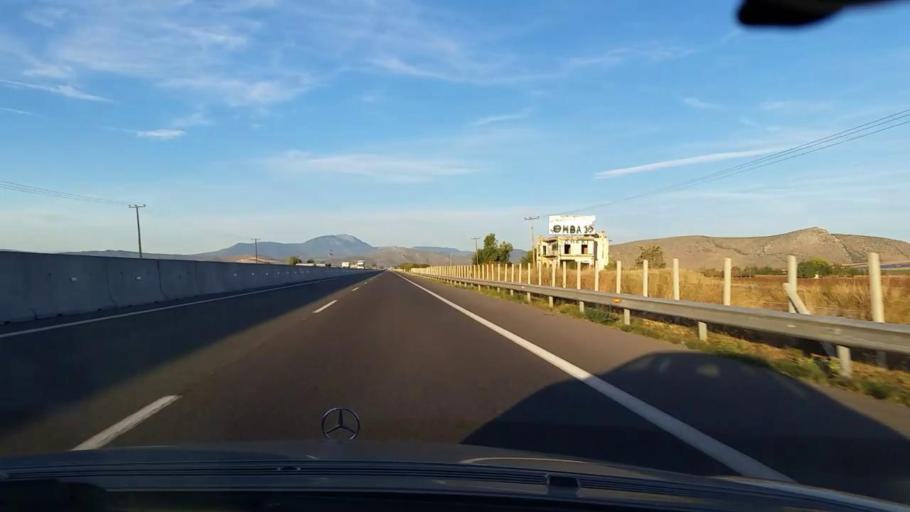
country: GR
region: Central Greece
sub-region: Nomos Voiotias
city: Thivai
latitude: 38.3688
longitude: 23.3637
